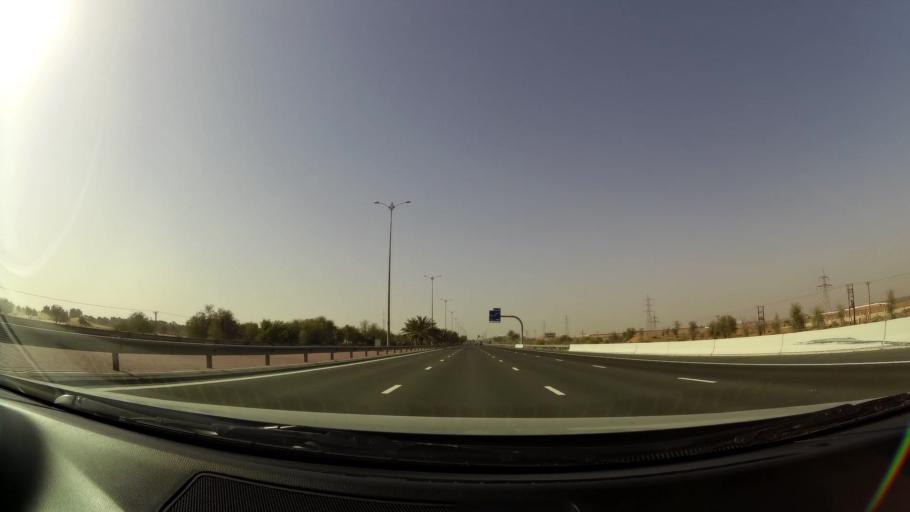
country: OM
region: Al Buraimi
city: Al Buraymi
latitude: 24.4991
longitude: 55.7687
